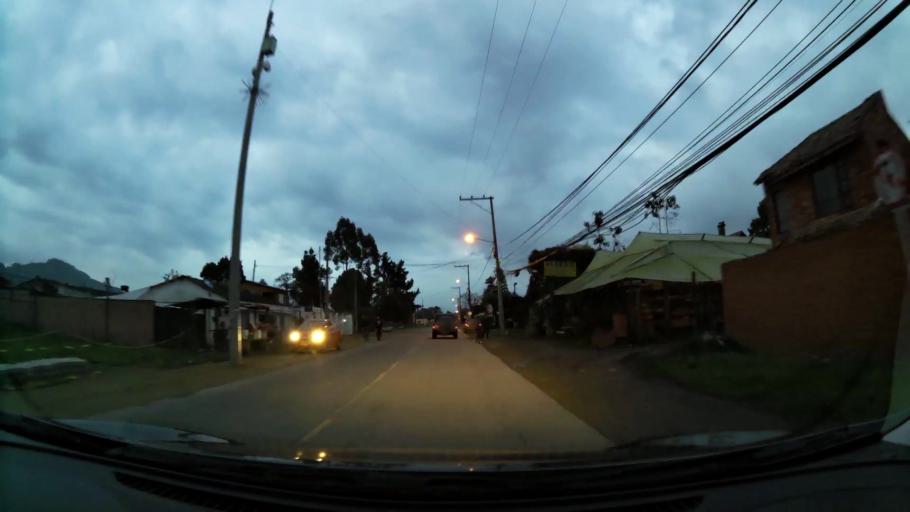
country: CO
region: Cundinamarca
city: Chia
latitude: 4.8422
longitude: -74.0672
